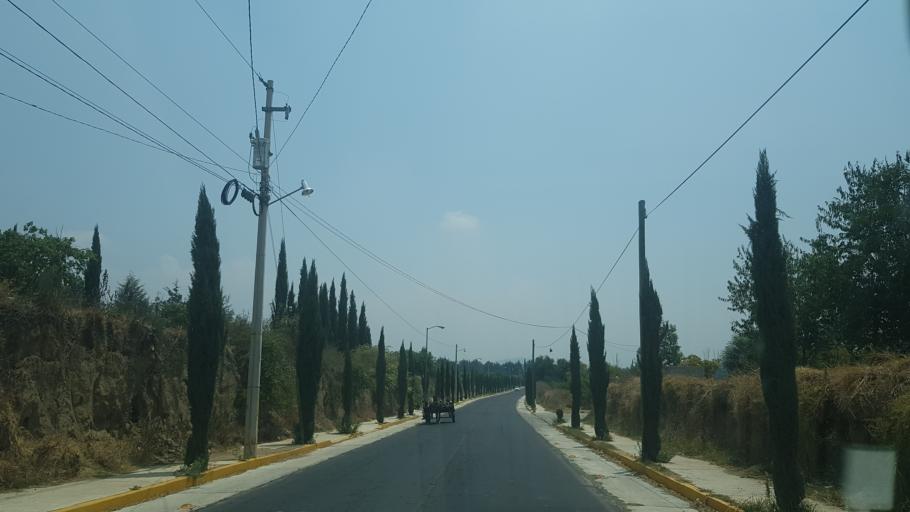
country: MX
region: Puebla
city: San Andres Calpan
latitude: 19.1032
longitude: -98.4477
